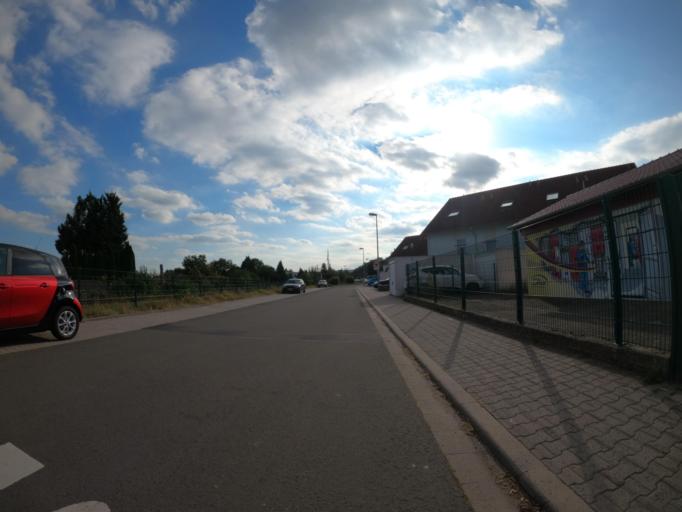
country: DE
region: Rheinland-Pfalz
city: Grunstadt
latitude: 49.5699
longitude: 8.1701
